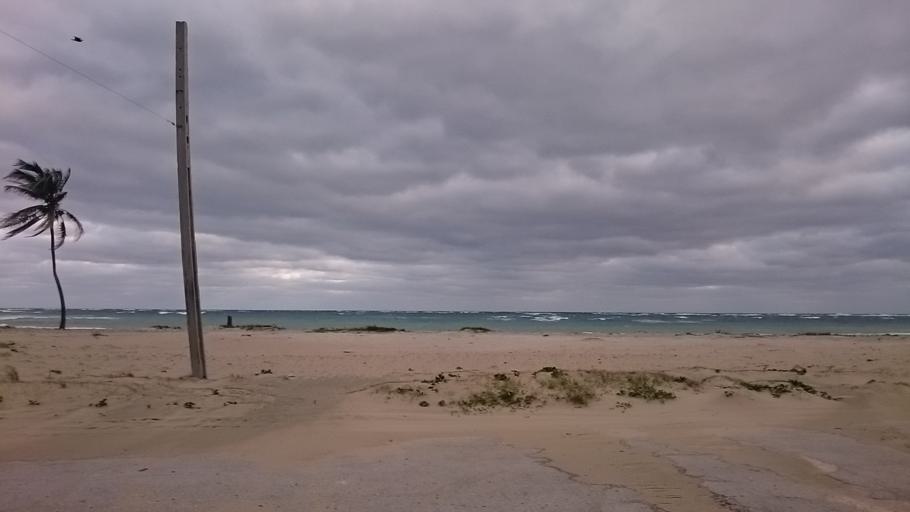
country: CU
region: Mayabeque
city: Jaruco
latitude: 23.1734
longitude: -82.1111
